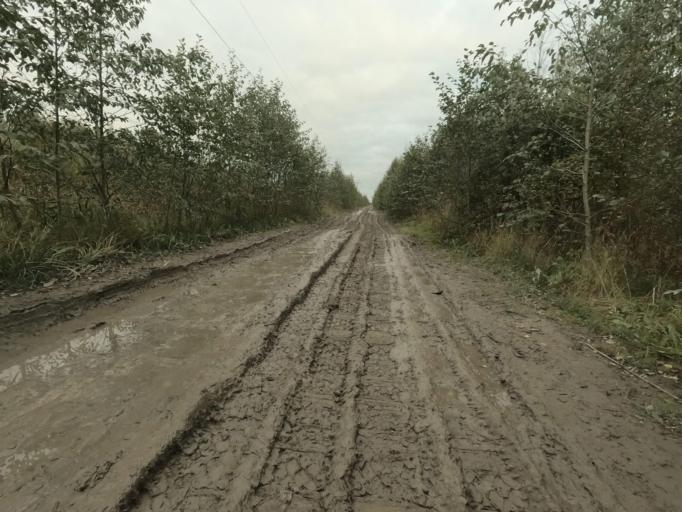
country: RU
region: St.-Petersburg
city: Sapernyy
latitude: 59.7543
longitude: 30.6961
